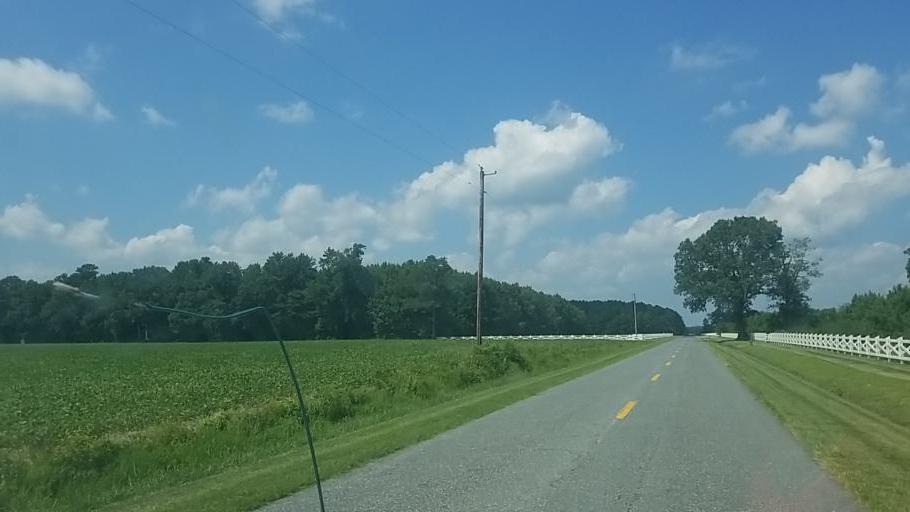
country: US
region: Maryland
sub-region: Wicomico County
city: Hebron
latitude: 38.4501
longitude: -75.8490
